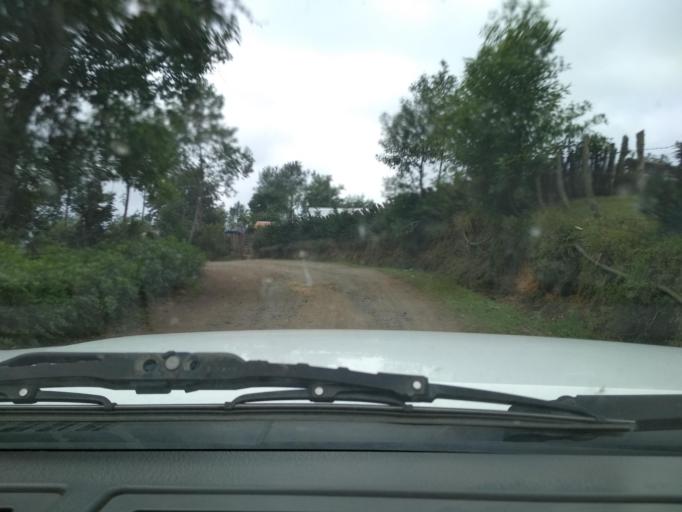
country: MX
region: Veracruz
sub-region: La Perla
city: Chilapa
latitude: 18.9948
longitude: -97.1685
